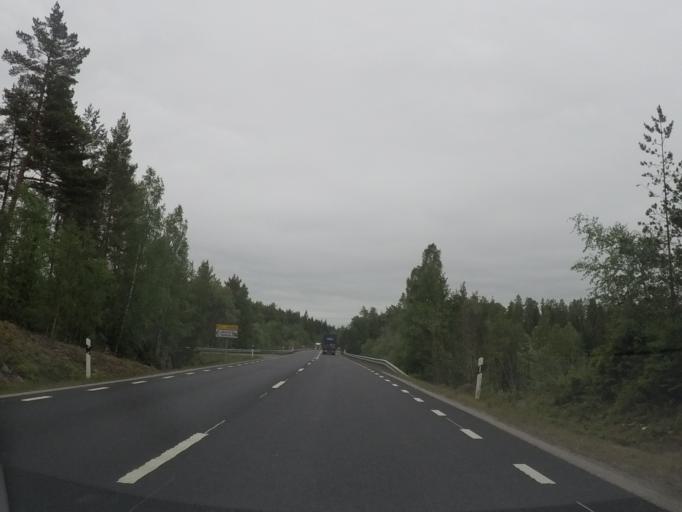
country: SE
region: Soedermanland
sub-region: Flens Kommun
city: Flen
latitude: 59.0652
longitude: 16.6199
